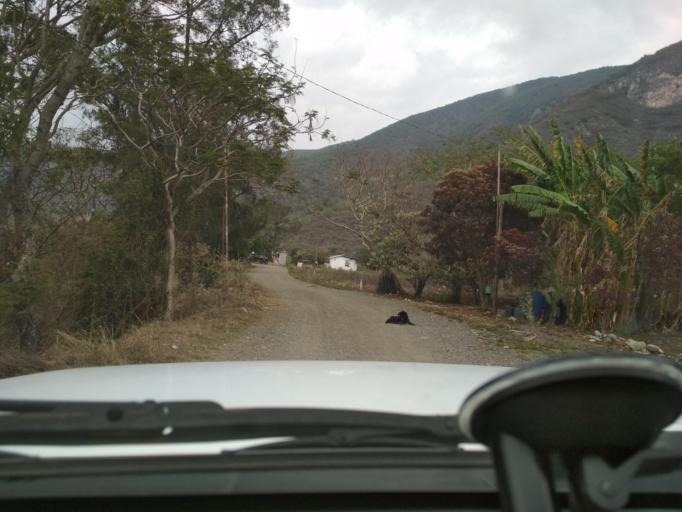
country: MX
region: Veracruz
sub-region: Nogales
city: Taza de Agua Ojo Zarco
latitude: 18.7894
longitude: -97.2149
